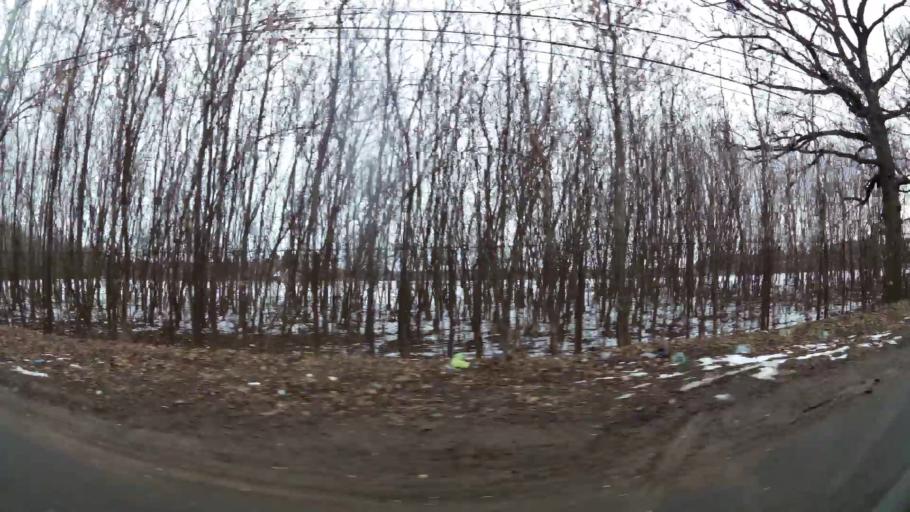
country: RO
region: Ilfov
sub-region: Comuna Pantelimon
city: Pantelimon
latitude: 44.4654
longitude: 26.2116
